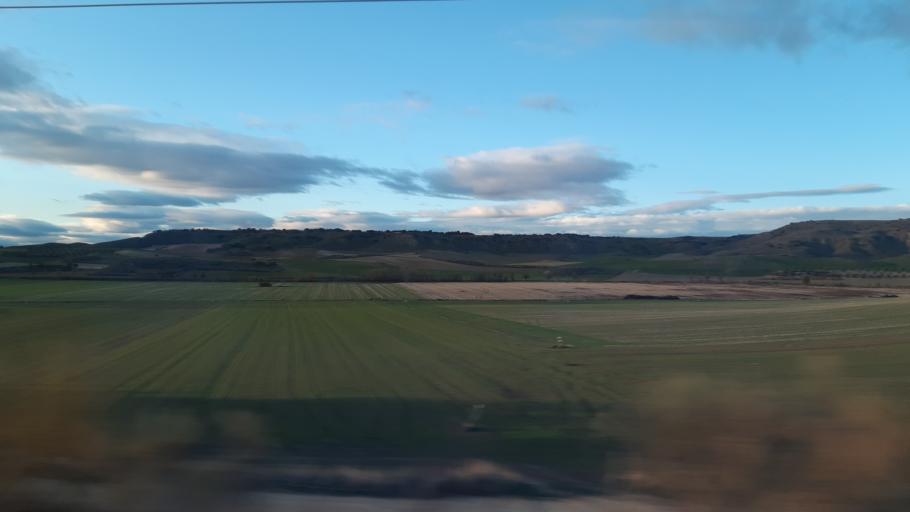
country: ES
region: Madrid
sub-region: Provincia de Madrid
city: Villalbilla
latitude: 40.4606
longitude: -3.3020
